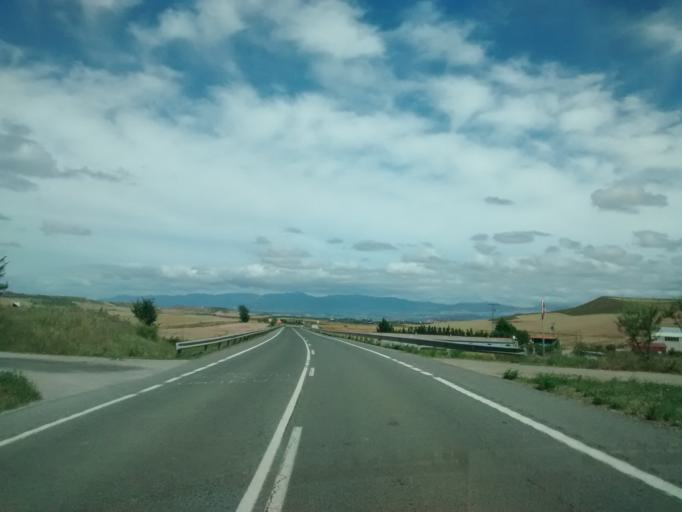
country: ES
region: La Rioja
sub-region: Provincia de La Rioja
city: Clavijo
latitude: 42.3762
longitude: -2.3898
